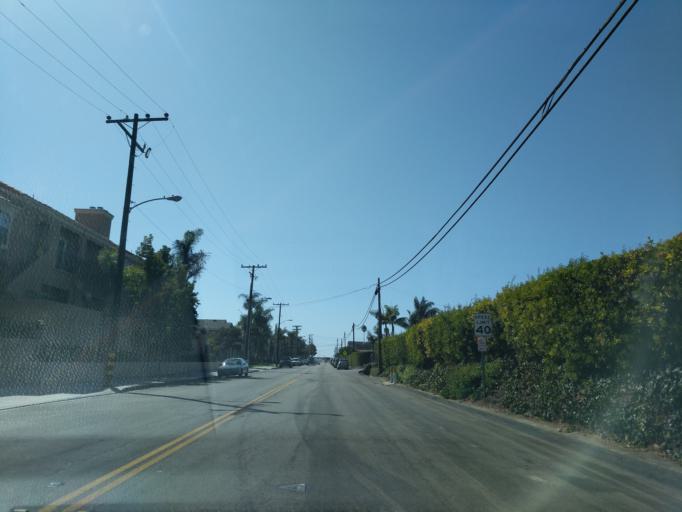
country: US
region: California
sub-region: Orange County
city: Newport Beach
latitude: 33.6289
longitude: -117.9323
